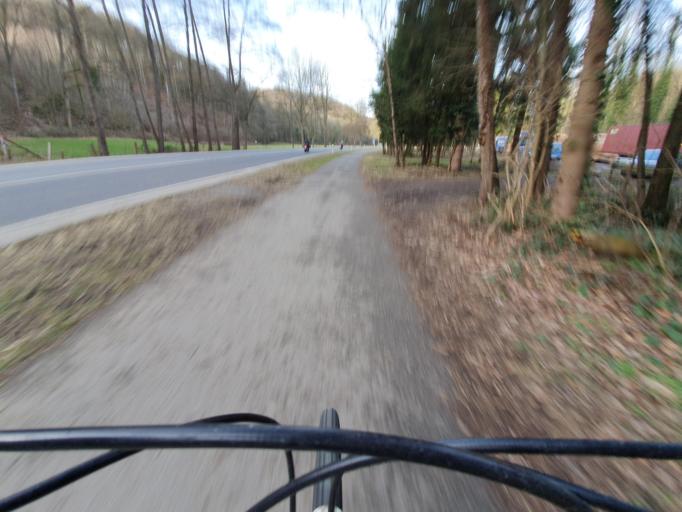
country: DE
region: North Rhine-Westphalia
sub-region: Regierungsbezirk Koln
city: Odenthal
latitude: 51.0445
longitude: 7.1235
